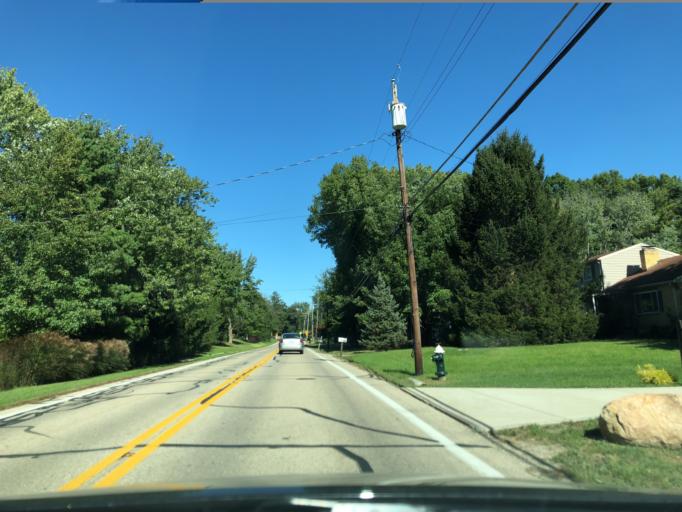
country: US
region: Ohio
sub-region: Hamilton County
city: Sixteen Mile Stand
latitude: 39.2790
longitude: -84.3113
